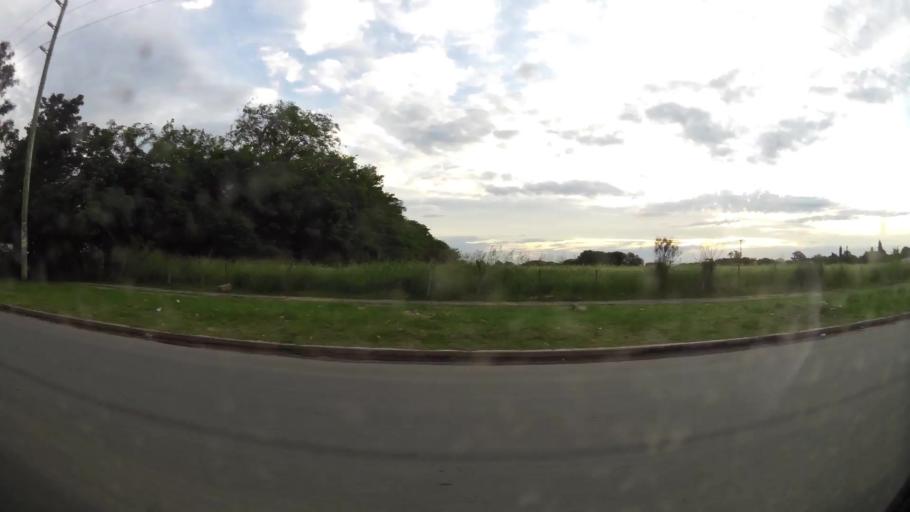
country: AR
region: Buenos Aires
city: San Nicolas de los Arroyos
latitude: -33.3221
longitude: -60.2431
